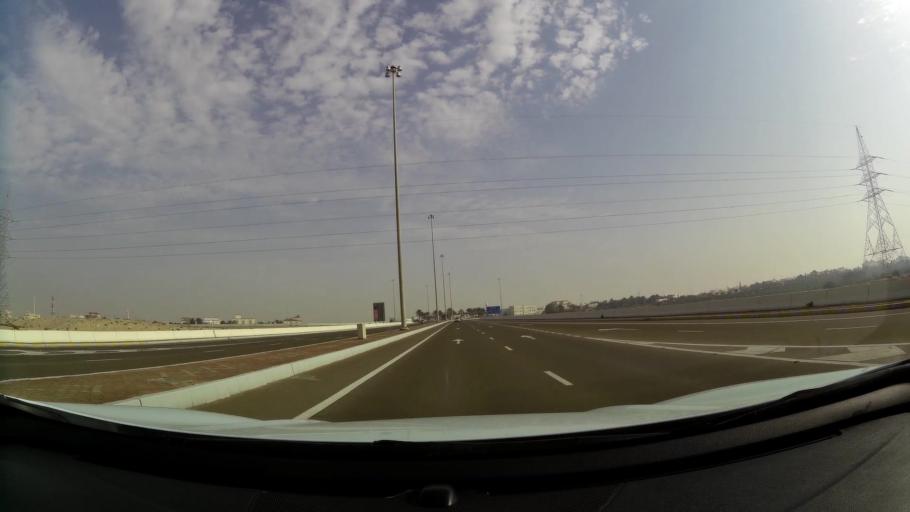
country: AE
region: Abu Dhabi
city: Abu Dhabi
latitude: 24.2534
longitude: 54.7091
